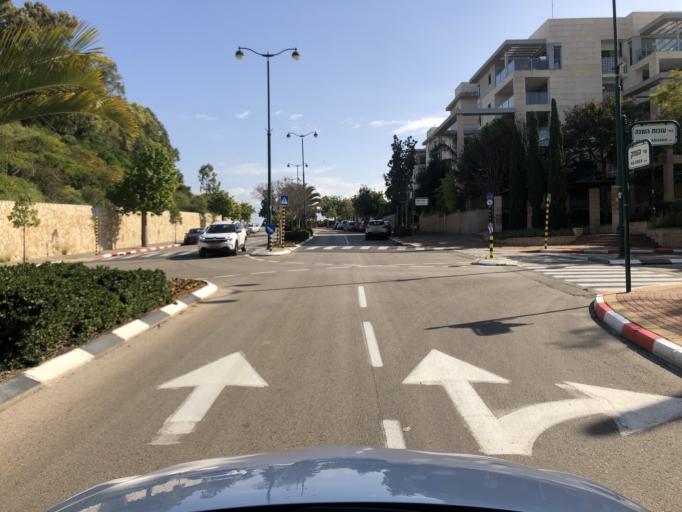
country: IL
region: Central District
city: Ness Ziona
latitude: 31.9143
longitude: 34.7910
